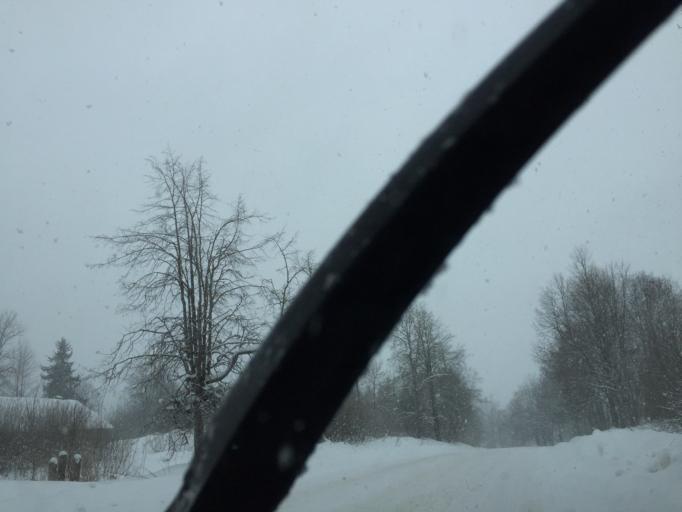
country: LV
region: Amatas Novads
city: Drabesi
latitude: 57.0656
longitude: 25.3075
